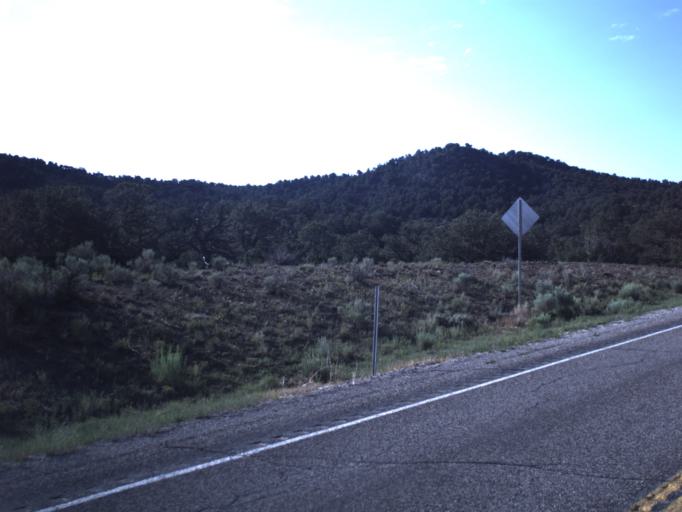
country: US
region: Utah
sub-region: Wayne County
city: Loa
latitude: 38.7214
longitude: -111.3983
